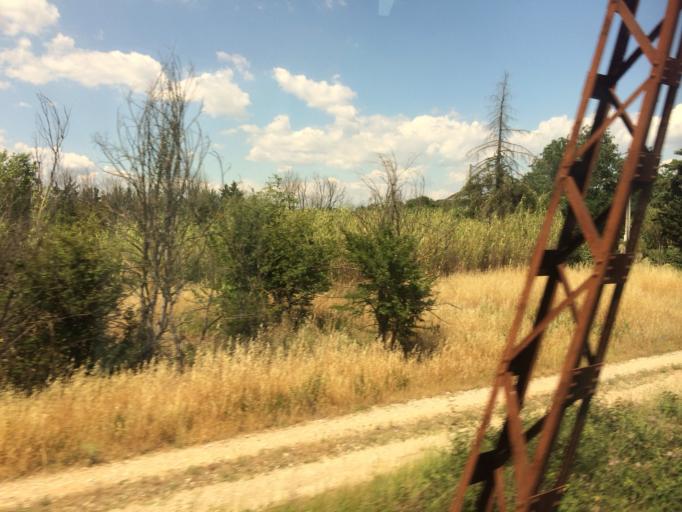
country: FR
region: Languedoc-Roussillon
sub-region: Departement de l'Herault
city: Valergues
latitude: 43.6754
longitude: 4.0672
